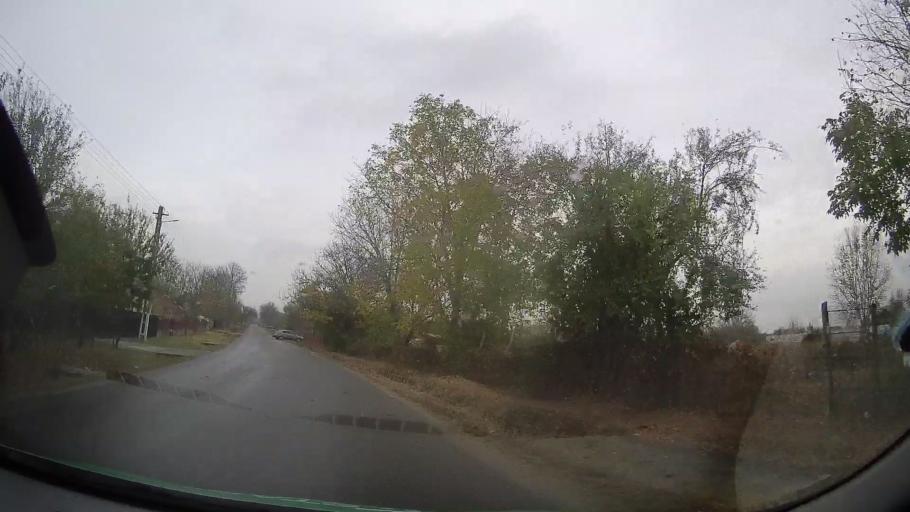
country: RO
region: Prahova
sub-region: Comuna Gherghita
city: Gherghita
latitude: 44.7988
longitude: 26.2862
